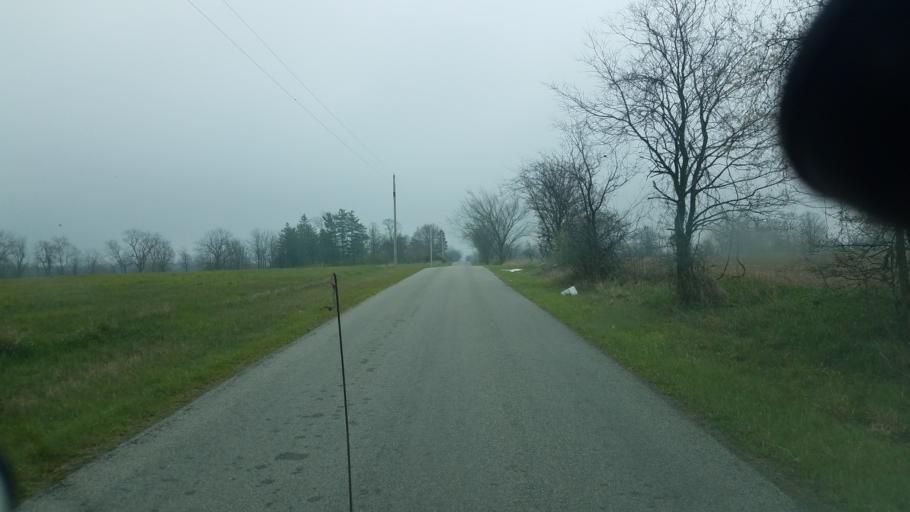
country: US
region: Ohio
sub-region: Logan County
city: Northwood
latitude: 40.4314
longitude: -83.7777
